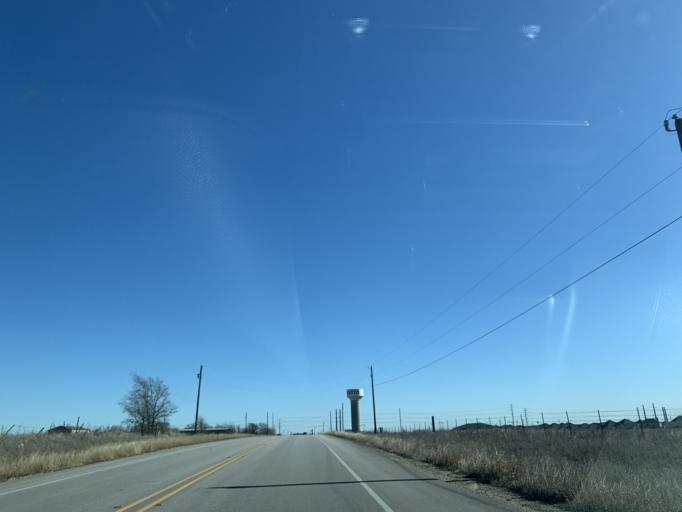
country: US
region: Texas
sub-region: Williamson County
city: Hutto
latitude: 30.5583
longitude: -97.5679
